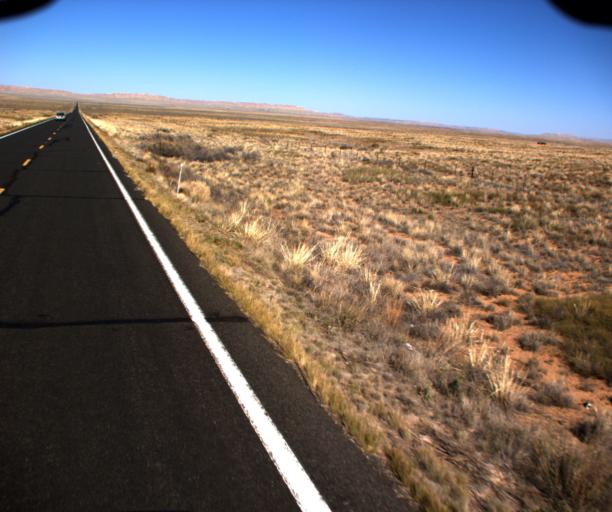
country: US
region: Arizona
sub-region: Navajo County
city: First Mesa
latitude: 35.6700
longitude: -110.4964
